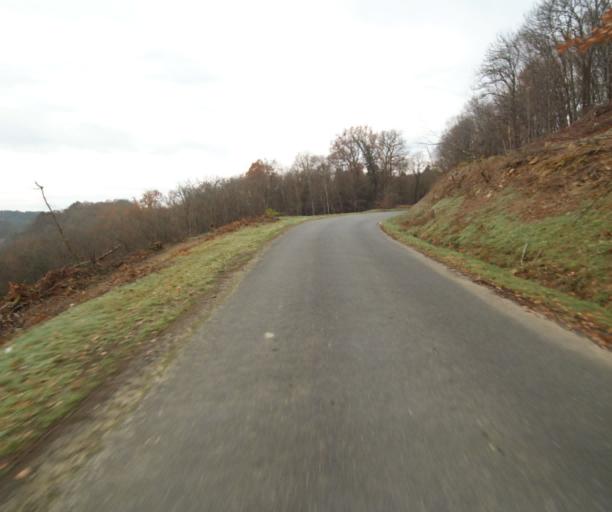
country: FR
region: Limousin
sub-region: Departement de la Correze
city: Chameyrat
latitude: 45.2391
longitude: 1.7318
